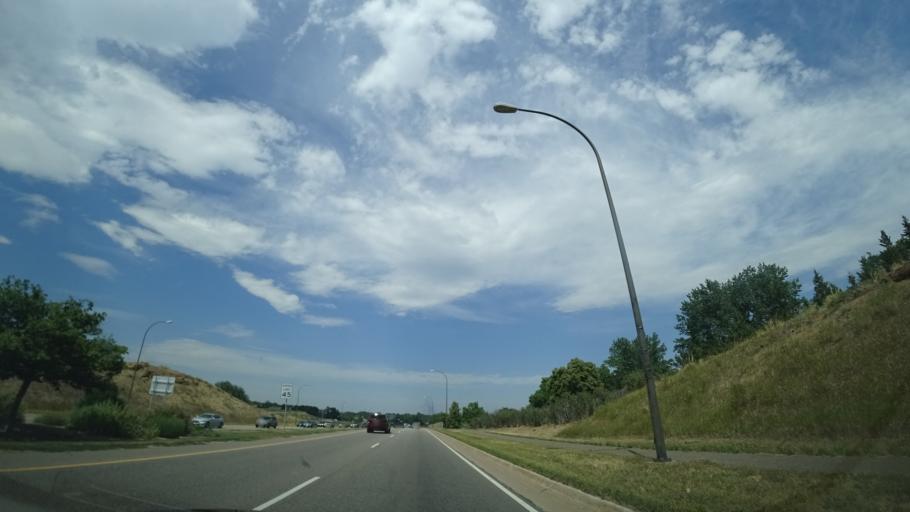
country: US
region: Colorado
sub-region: Jefferson County
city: Lakewood
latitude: 39.6909
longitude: -105.1160
